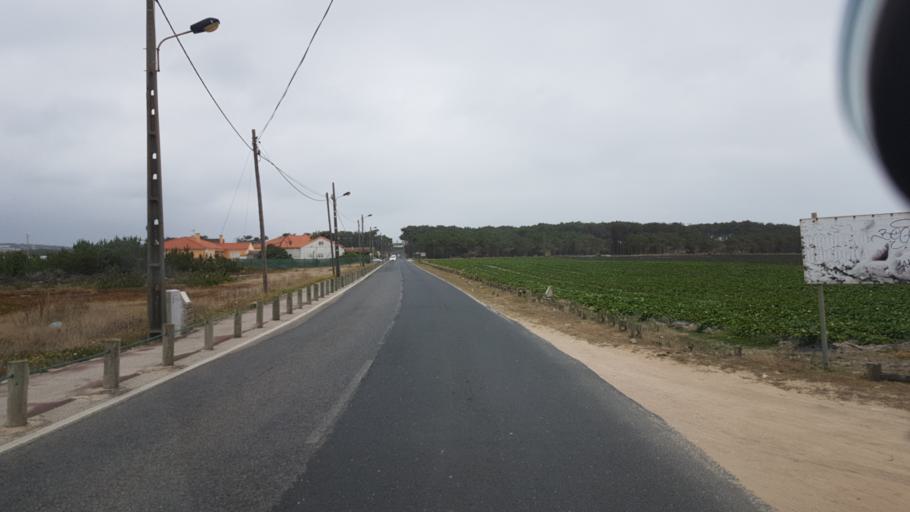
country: PT
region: Lisbon
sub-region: Torres Vedras
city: Silveira
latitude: 39.1595
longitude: -9.3618
